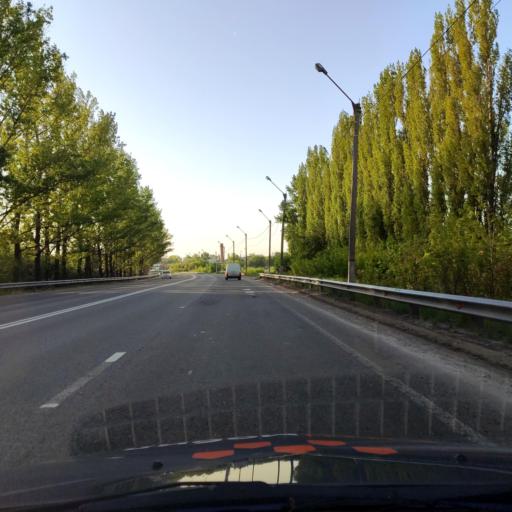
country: RU
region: Lipetsk
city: Yelets
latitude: 52.5987
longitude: 38.4746
